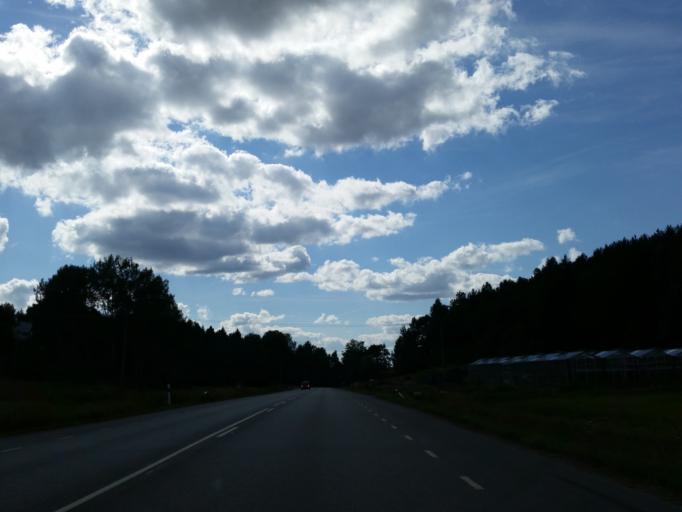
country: SE
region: Soedermanland
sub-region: Trosa Kommun
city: Vagnharad
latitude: 58.9474
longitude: 17.5361
